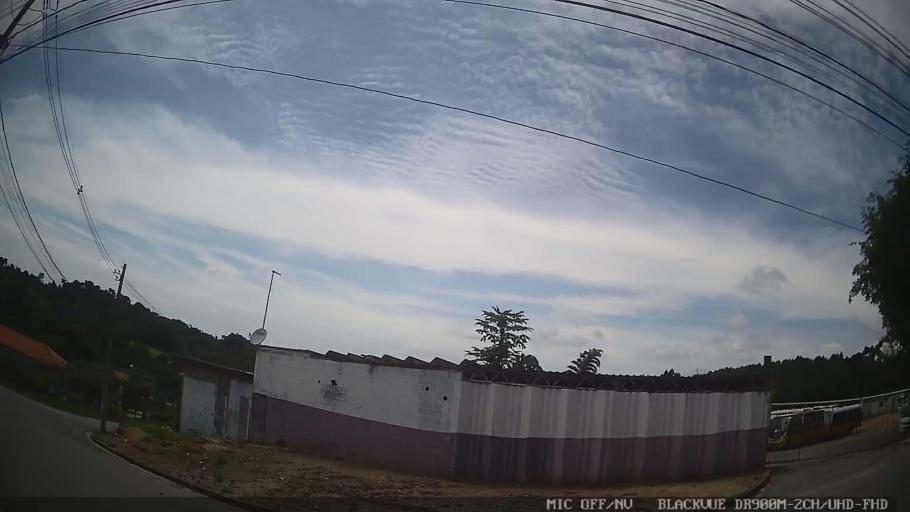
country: BR
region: Sao Paulo
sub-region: Santa Isabel
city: Santa Isabel
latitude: -23.4148
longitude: -46.2080
